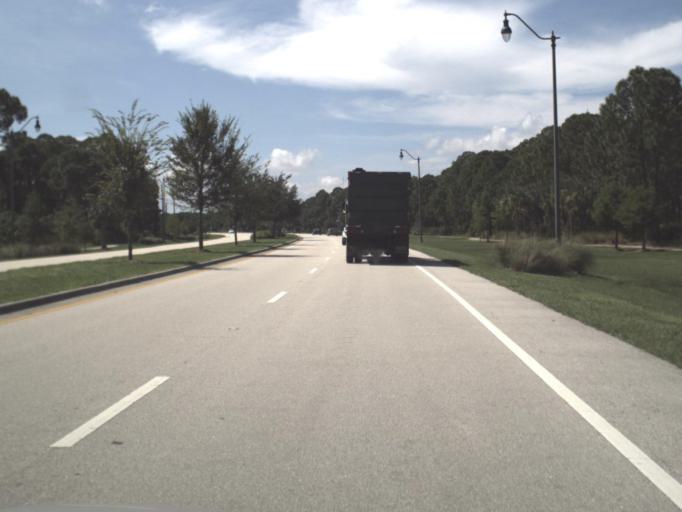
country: US
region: Florida
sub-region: Sarasota County
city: North Port
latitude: 27.0428
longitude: -82.1613
